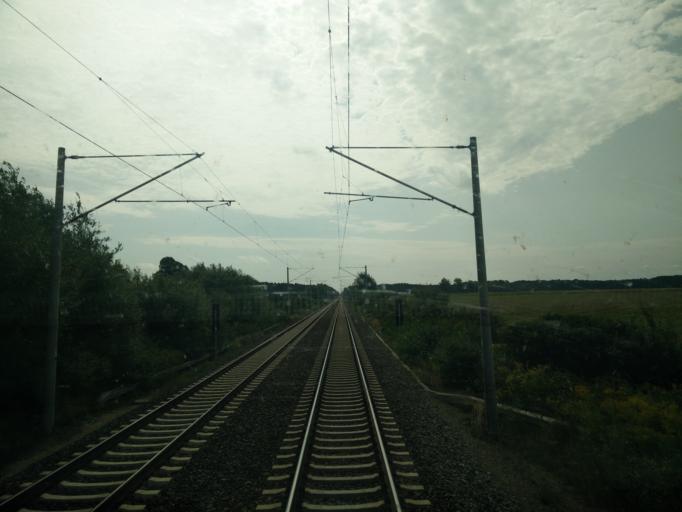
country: DE
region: Brandenburg
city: Luebben
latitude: 51.9225
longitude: 13.8937
